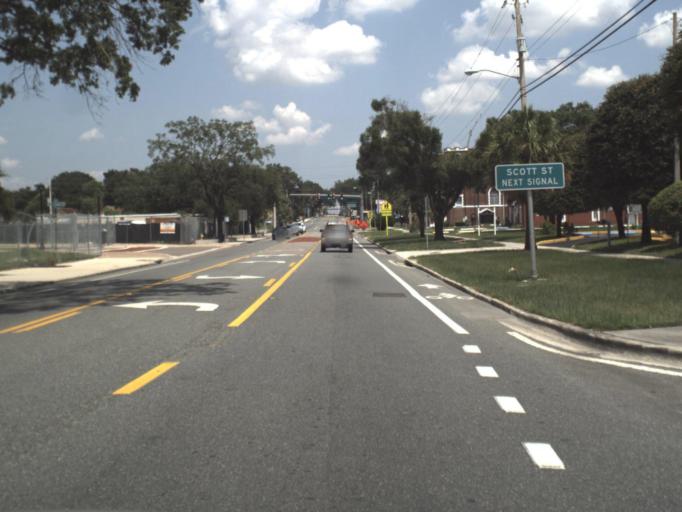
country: US
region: Florida
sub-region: Hillsborough County
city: Tampa
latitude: 27.9548
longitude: -82.4512
